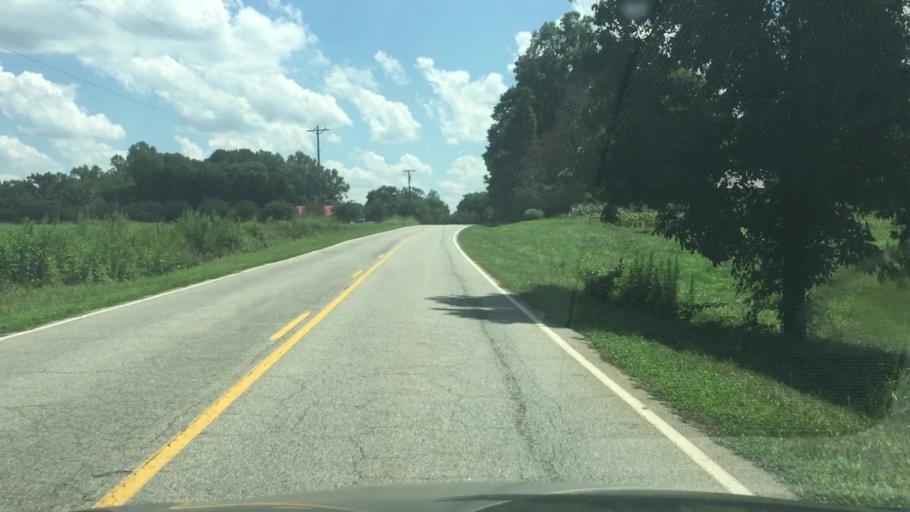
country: US
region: North Carolina
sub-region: Rowan County
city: China Grove
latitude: 35.6435
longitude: -80.6377
